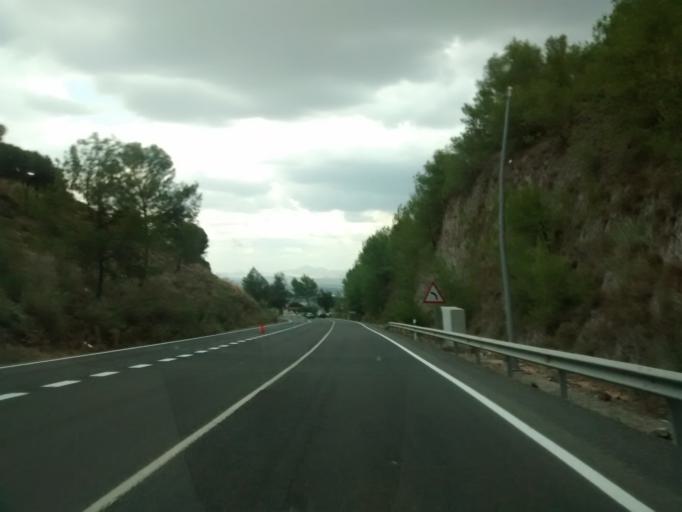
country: ES
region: Andalusia
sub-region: Provincia de Cadiz
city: Bornos
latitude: 36.8128
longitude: -5.7522
